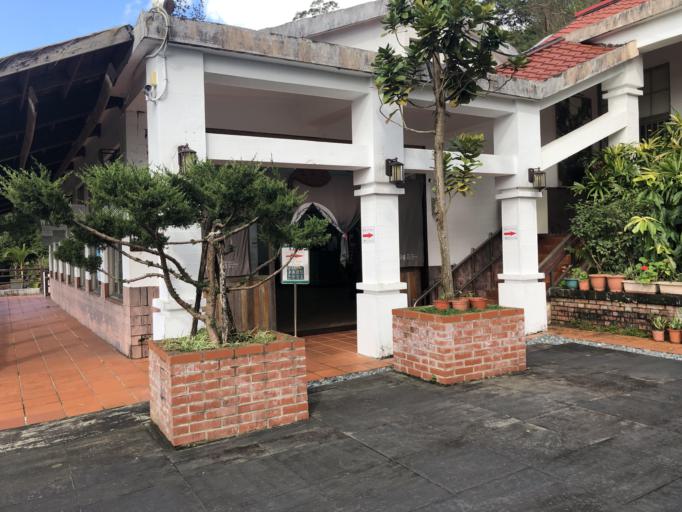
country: TW
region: Taiwan
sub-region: Keelung
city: Keelung
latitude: 25.0273
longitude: 121.6642
